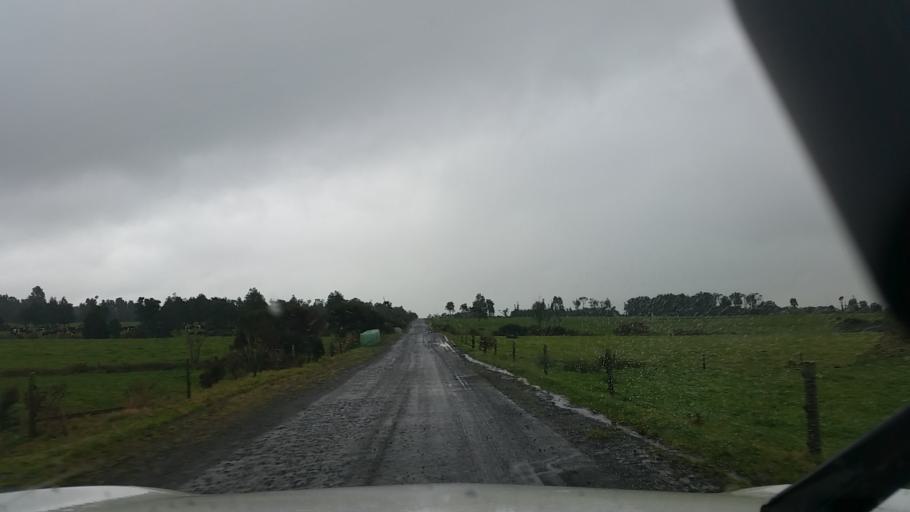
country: NZ
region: Taranaki
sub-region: South Taranaki District
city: Eltham
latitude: -39.2799
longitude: 174.1783
